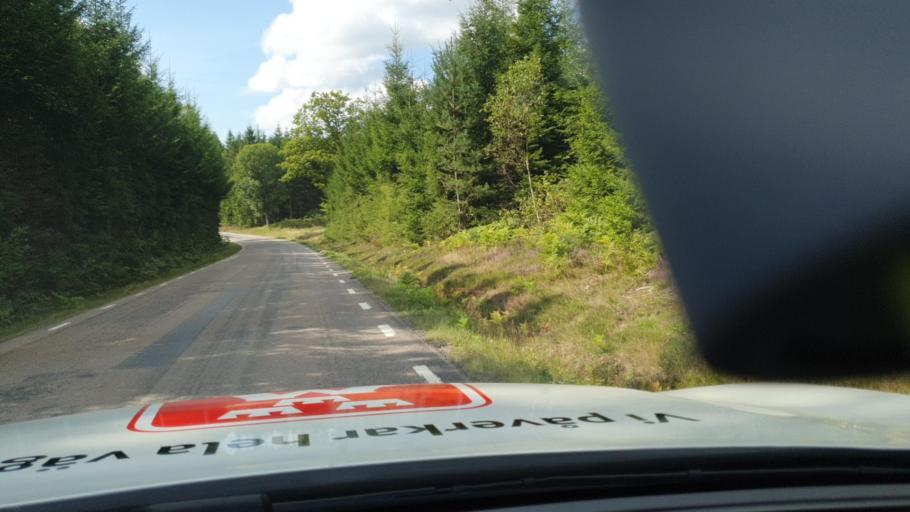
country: SE
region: Halland
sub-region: Laholms Kommun
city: Knared
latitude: 56.4937
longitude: 13.2985
